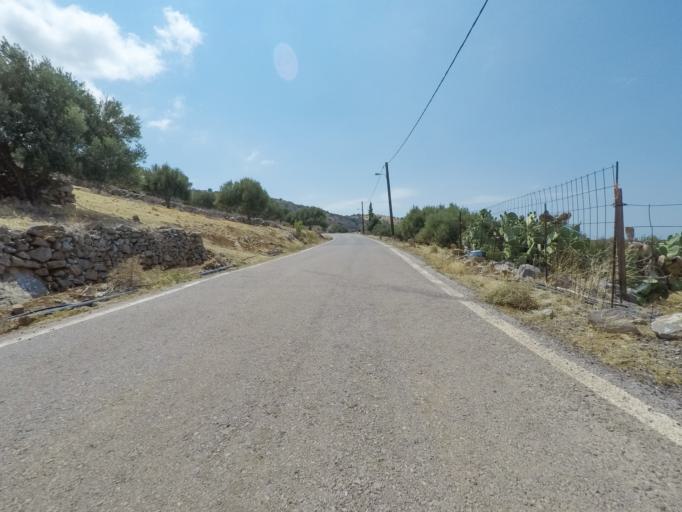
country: GR
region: Crete
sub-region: Nomos Lasithiou
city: Elounda
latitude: 35.3178
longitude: 25.6810
